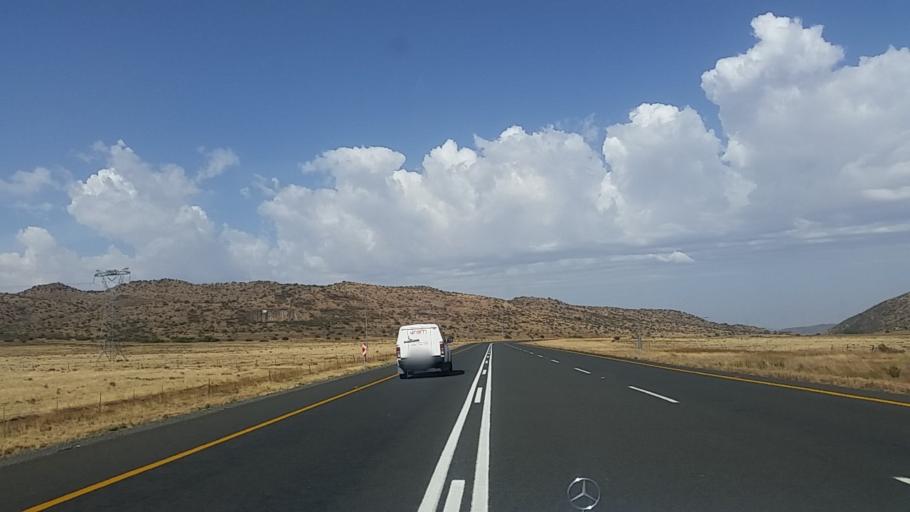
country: ZA
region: Northern Cape
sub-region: Pixley ka Seme District Municipality
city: Colesberg
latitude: -30.5309
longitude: 25.5383
